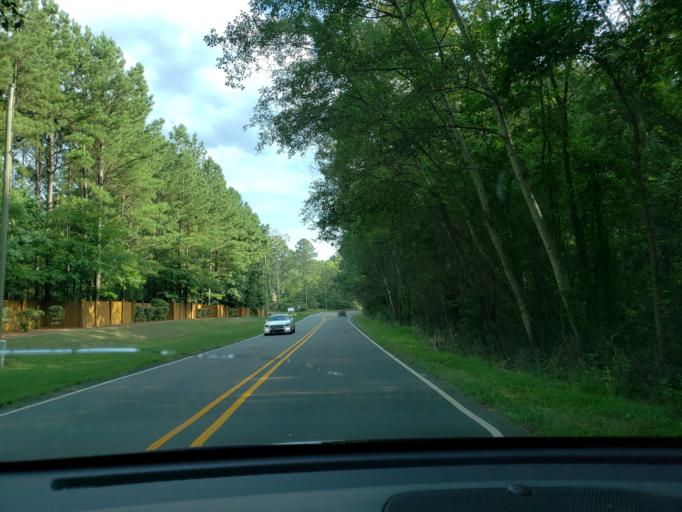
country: US
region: North Carolina
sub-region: Orange County
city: Chapel Hill
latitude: 35.8940
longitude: -78.9806
